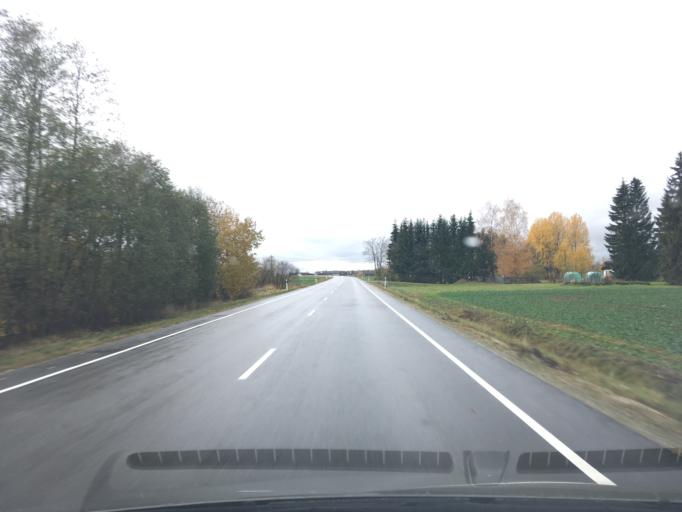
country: EE
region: Jogevamaa
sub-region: Tabivere vald
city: Tabivere
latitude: 58.4608
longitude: 26.5427
